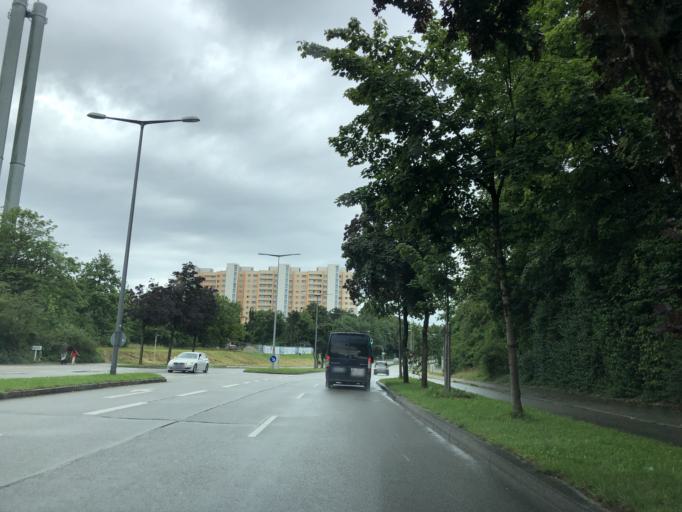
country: DE
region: Bavaria
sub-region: Upper Bavaria
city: Neubiberg
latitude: 48.1024
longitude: 11.6589
